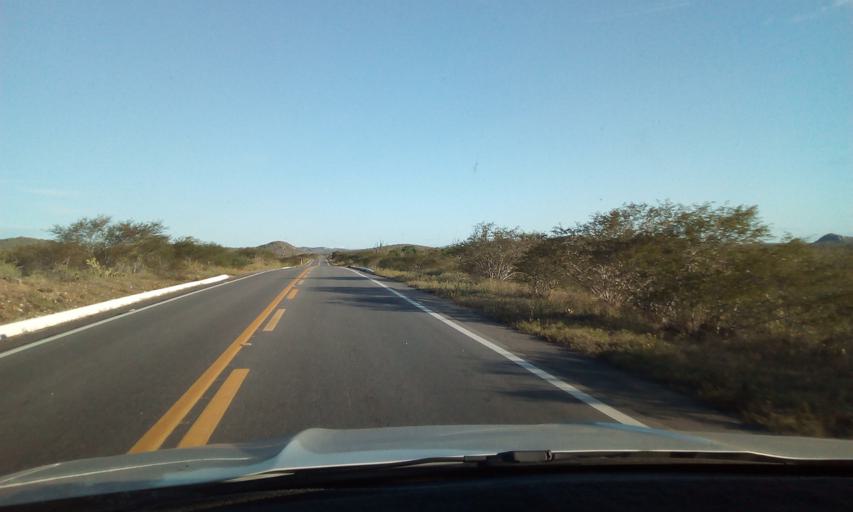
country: BR
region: Paraiba
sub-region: Areia
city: Remigio
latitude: -6.8602
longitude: -35.9258
